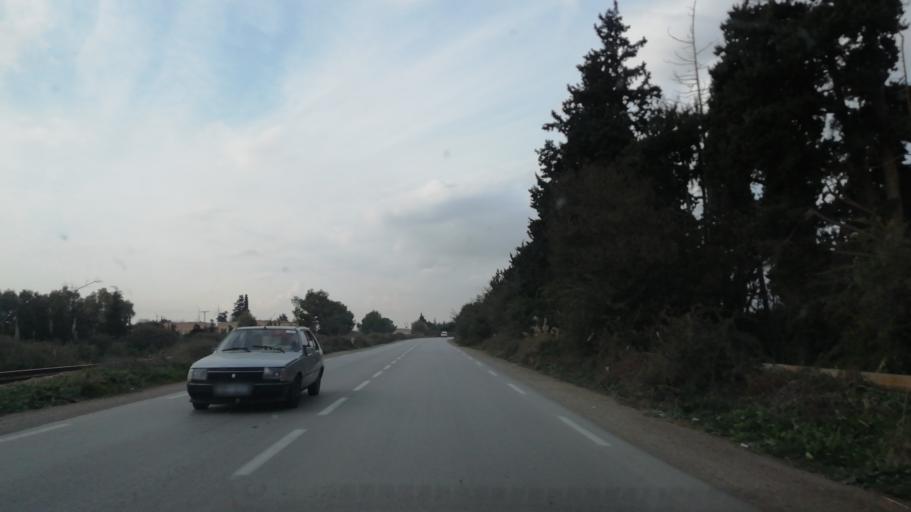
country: DZ
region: Mascara
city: Sig
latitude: 35.6654
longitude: 0.0019
